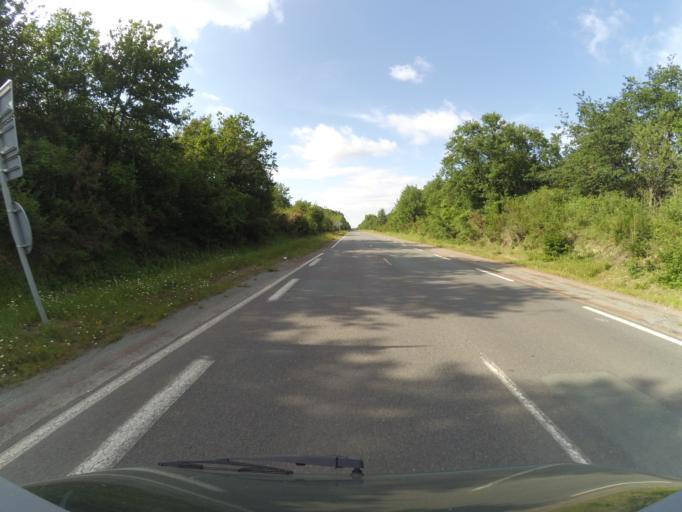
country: FR
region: Poitou-Charentes
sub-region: Departement de la Charente-Maritime
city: Le Gua
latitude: 45.7863
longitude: -0.9362
